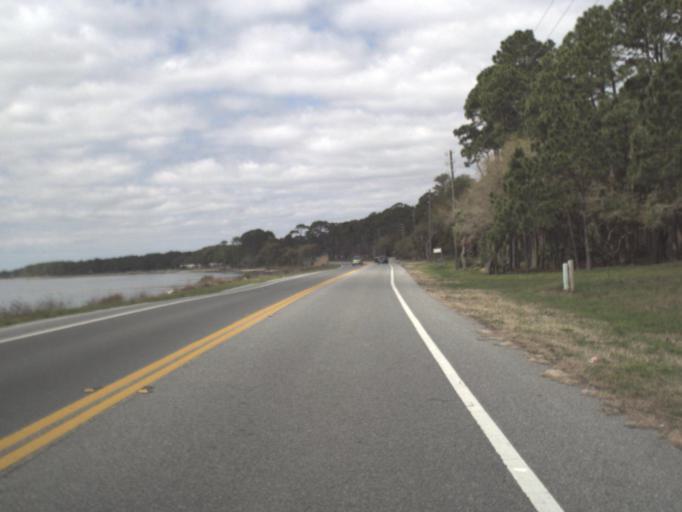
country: US
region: Florida
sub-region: Franklin County
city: Eastpoint
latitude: 29.7582
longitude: -84.8266
